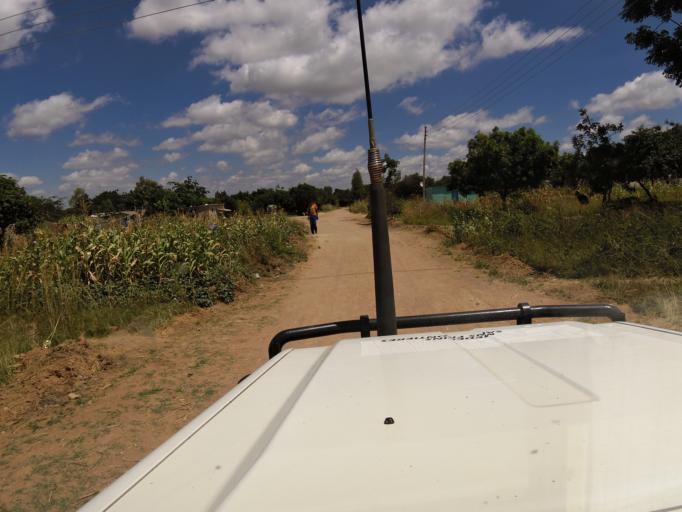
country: ZW
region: Harare
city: Epworth
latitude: -17.9024
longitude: 31.1591
